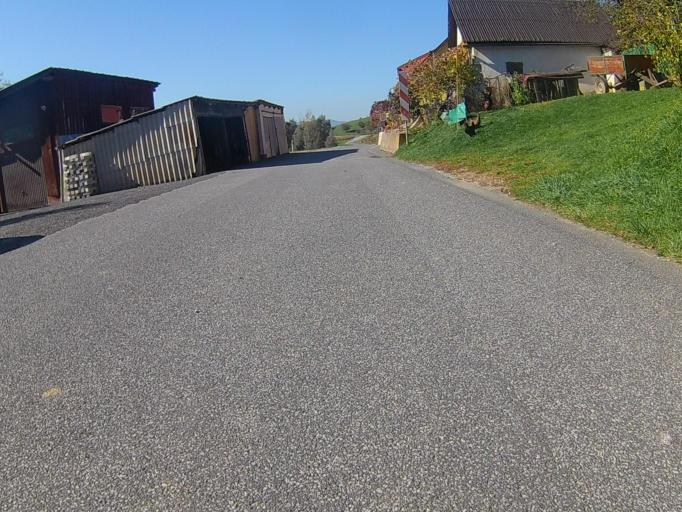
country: SI
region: Sveti Jurij v Slovenskih Goricah
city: Jurovski Dol
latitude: 46.5772
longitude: 15.7433
